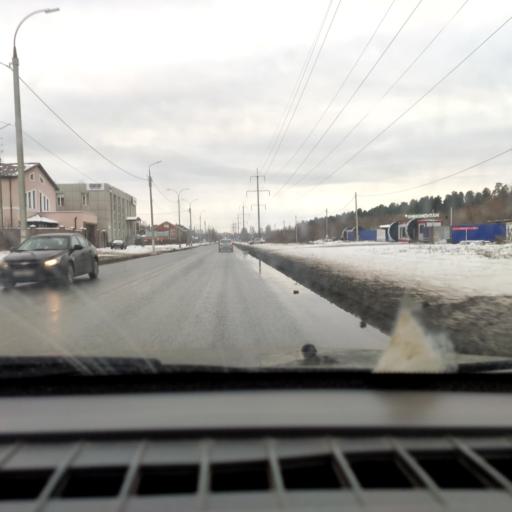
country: RU
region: Samara
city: Tol'yatti
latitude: 53.5211
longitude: 49.3952
